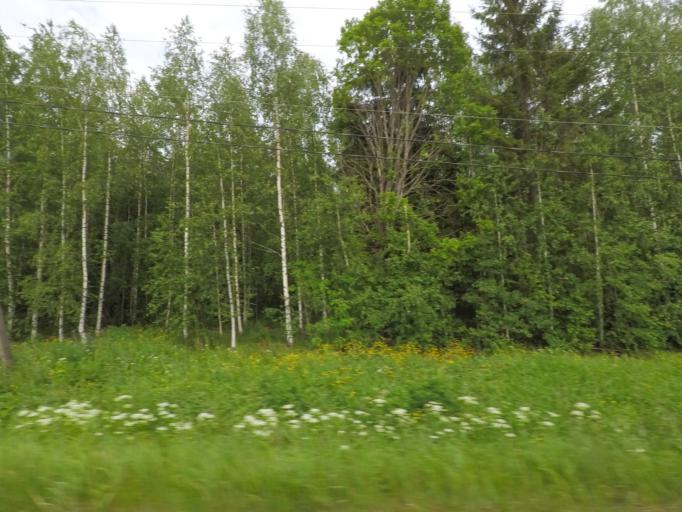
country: FI
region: Paijanne Tavastia
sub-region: Lahti
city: Hollola
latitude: 60.8797
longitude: 25.5054
